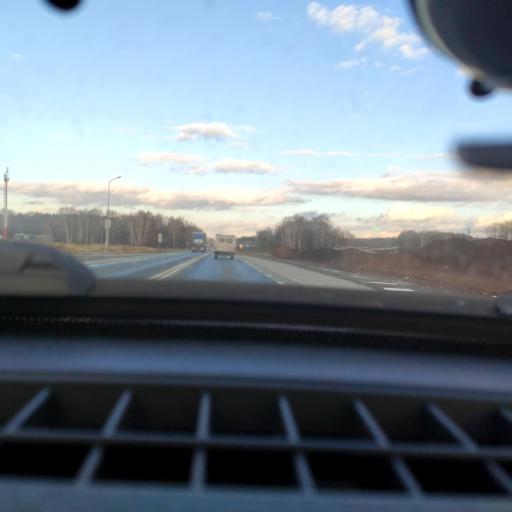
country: RU
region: Bashkortostan
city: Iglino
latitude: 54.7387
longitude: 56.2894
